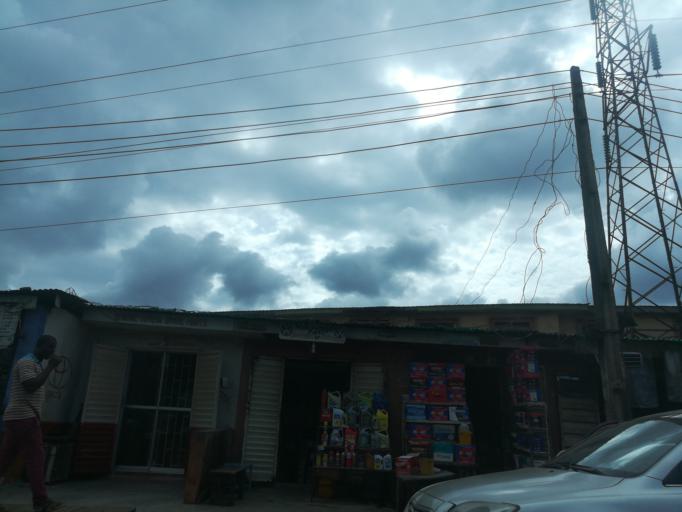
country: NG
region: Lagos
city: Agege
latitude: 6.6229
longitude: 3.3355
